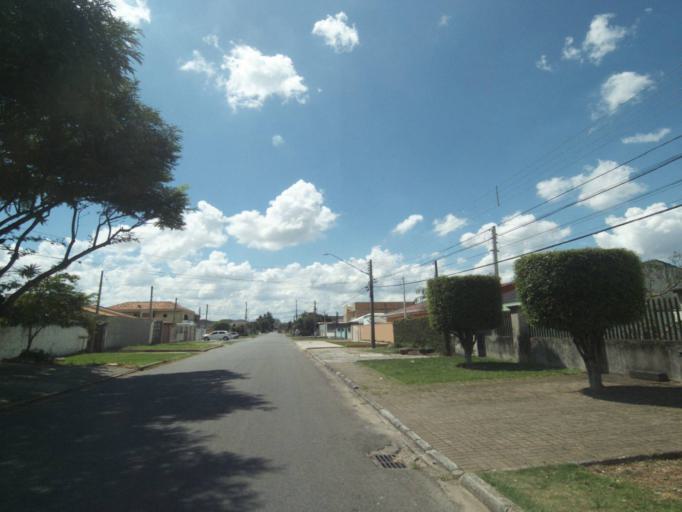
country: BR
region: Parana
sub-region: Pinhais
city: Pinhais
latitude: -25.4468
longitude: -49.2031
